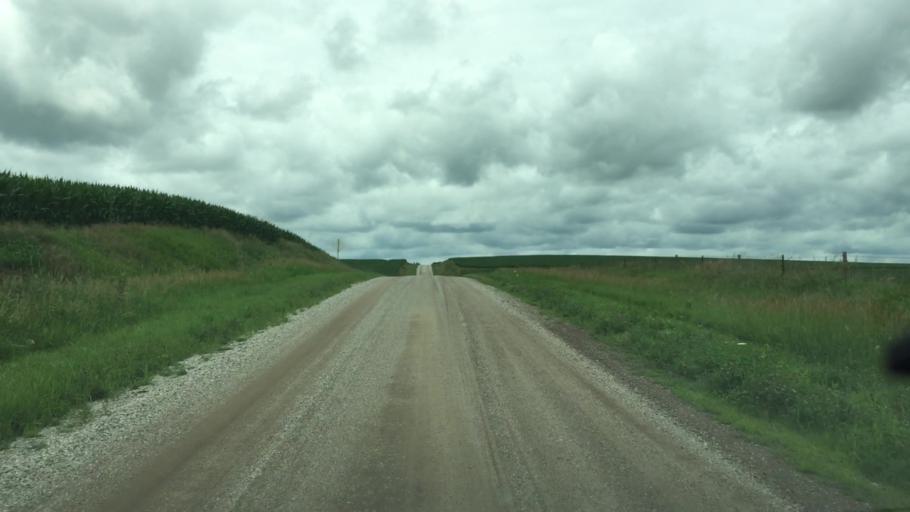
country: US
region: Iowa
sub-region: Jasper County
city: Monroe
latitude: 41.5953
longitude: -93.0988
